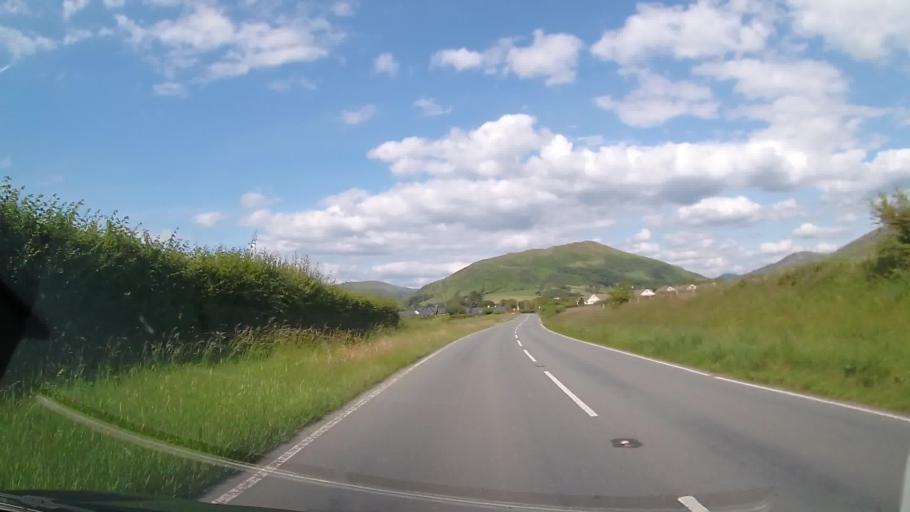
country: GB
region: Wales
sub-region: Gwynedd
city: Tywyn
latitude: 52.6034
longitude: -4.0596
